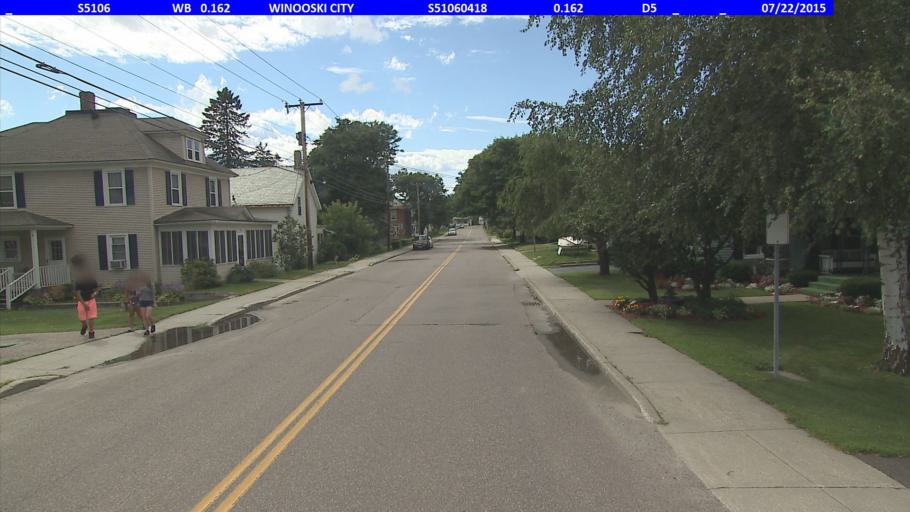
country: US
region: Vermont
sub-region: Chittenden County
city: Winooski
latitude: 44.4960
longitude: -73.1821
